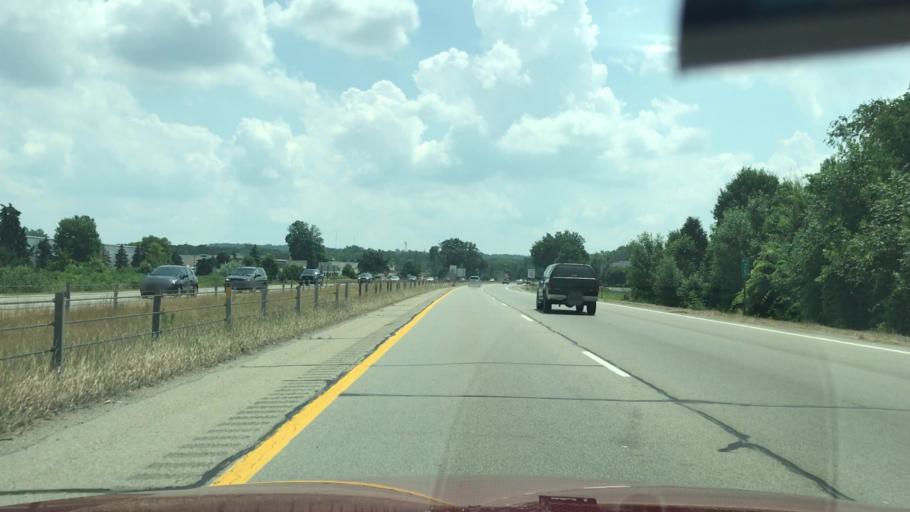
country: US
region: Michigan
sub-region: Kent County
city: Cutlerville
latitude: 42.8239
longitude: -85.6709
